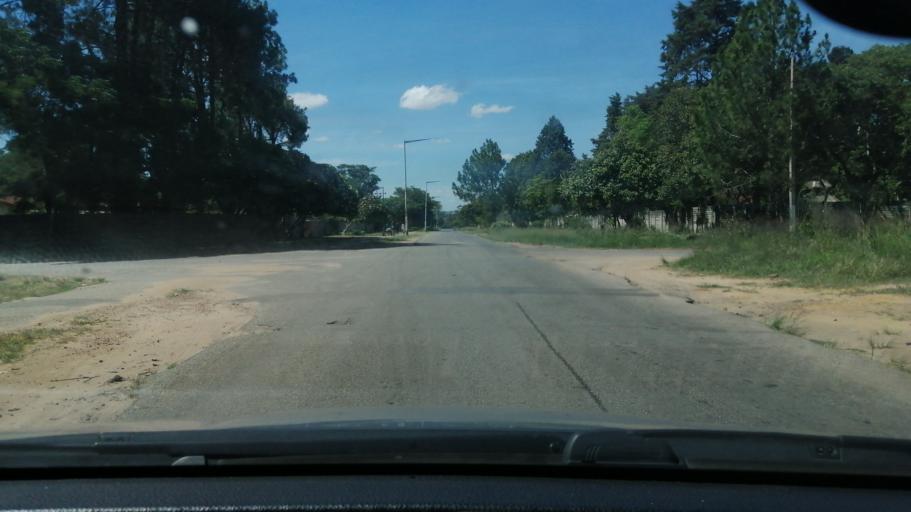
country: ZW
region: Harare
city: Epworth
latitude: -17.8268
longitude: 31.1254
